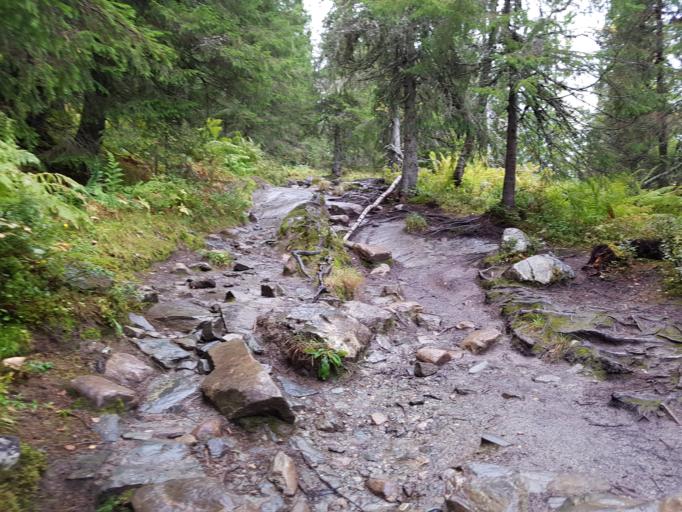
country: NO
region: Sor-Trondelag
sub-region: Melhus
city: Melhus
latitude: 63.4148
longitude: 10.2266
